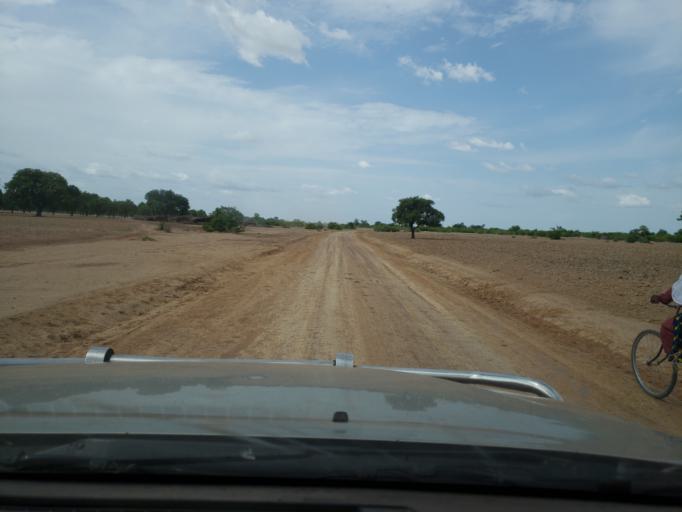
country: ML
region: Segou
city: Bla
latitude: 12.7444
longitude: -5.6372
